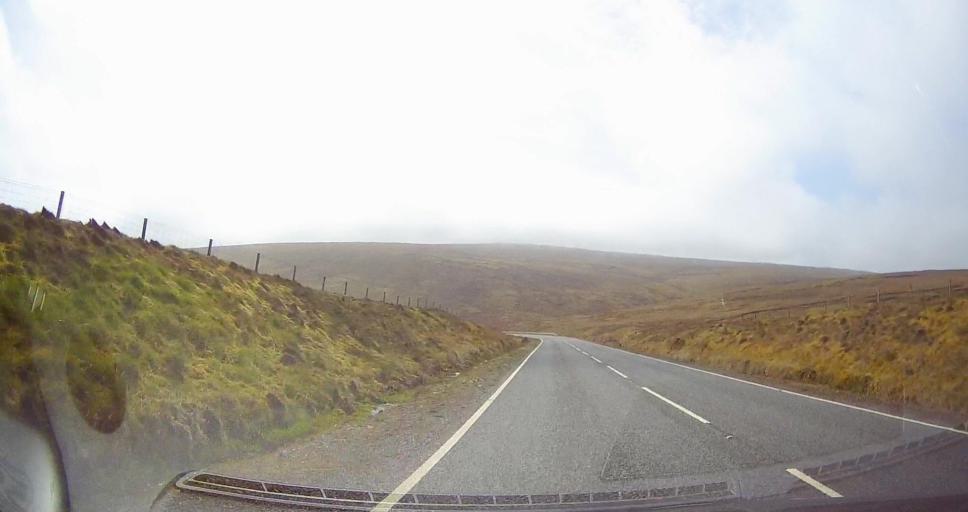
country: GB
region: Scotland
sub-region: Shetland Islands
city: Sandwick
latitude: 60.0074
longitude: -1.2728
